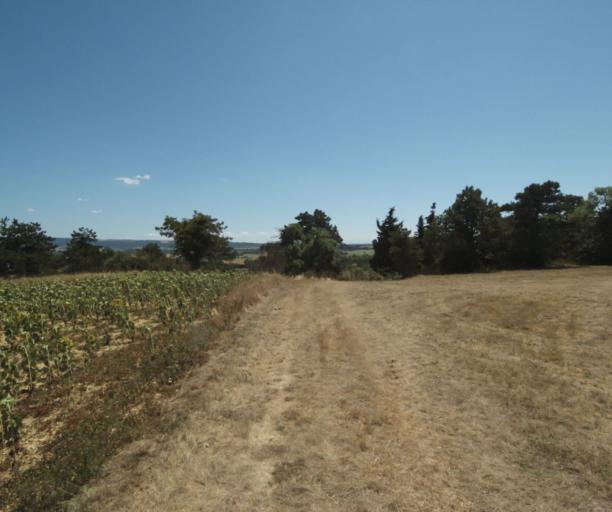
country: FR
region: Midi-Pyrenees
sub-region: Departement de la Haute-Garonne
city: Saint-Felix-Lauragais
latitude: 43.4558
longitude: 1.9082
